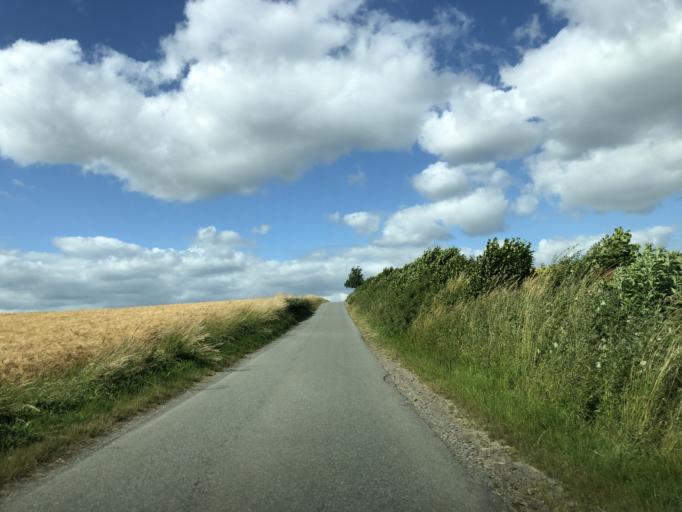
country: DK
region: South Denmark
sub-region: Vejle Kommune
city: Brejning
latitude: 55.6672
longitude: 9.6490
